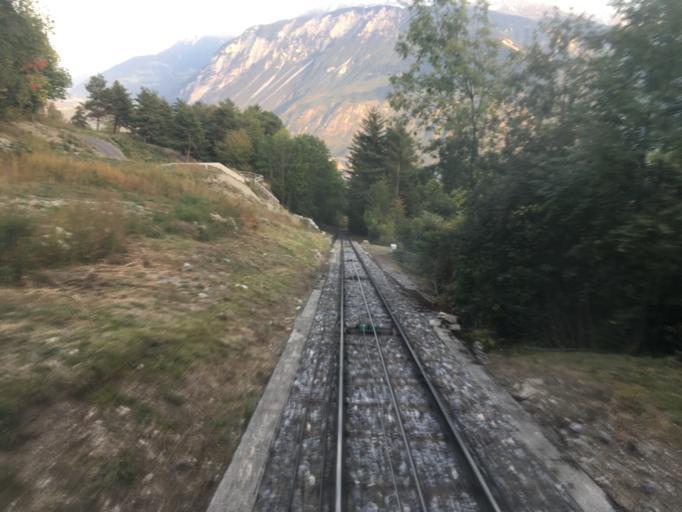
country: CH
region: Valais
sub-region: Sierre District
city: Randogne
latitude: 46.3077
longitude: 7.5035
